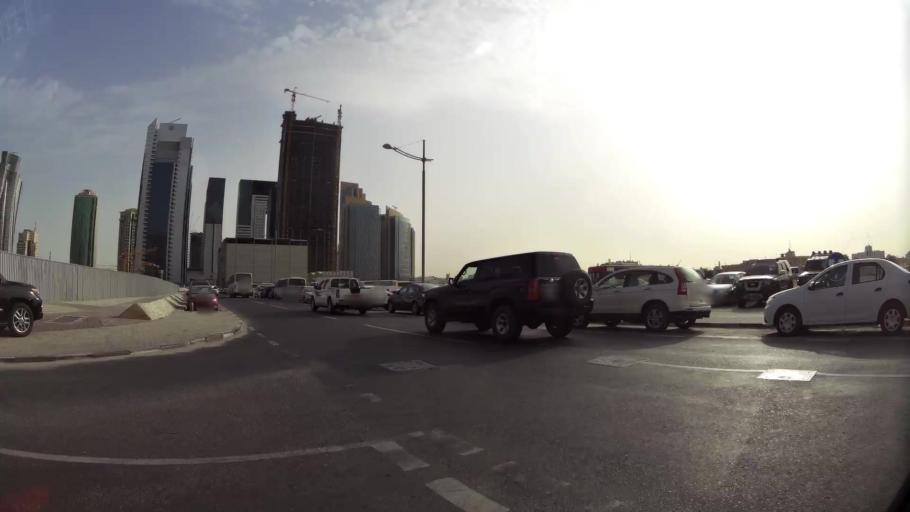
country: QA
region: Baladiyat ad Dawhah
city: Doha
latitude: 25.3241
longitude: 51.5220
